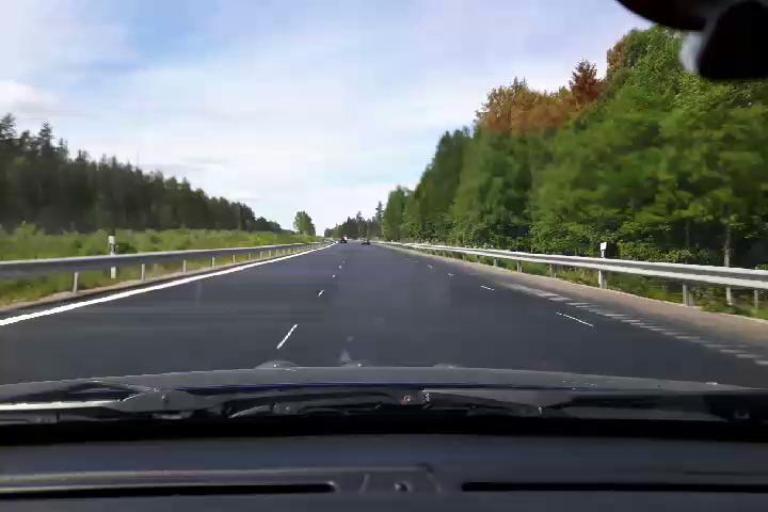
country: SE
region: Gaevleborg
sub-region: Gavle Kommun
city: Gavle
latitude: 60.6087
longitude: 17.1767
